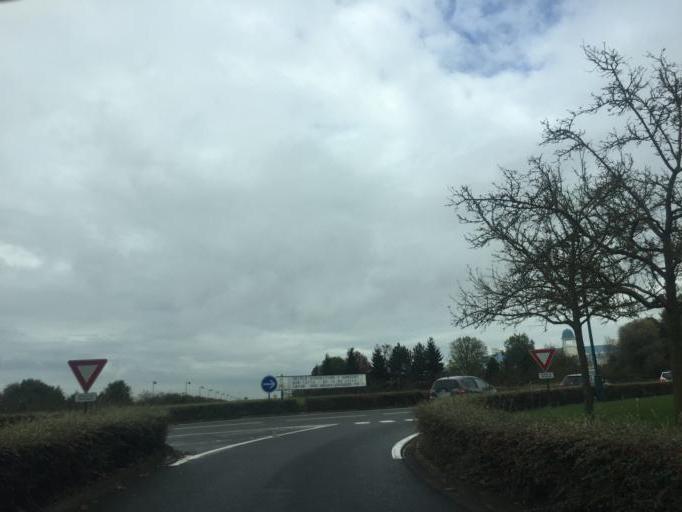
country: FR
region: Ile-de-France
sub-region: Departement de Seine-et-Marne
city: Serris
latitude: 48.8622
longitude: 2.7905
